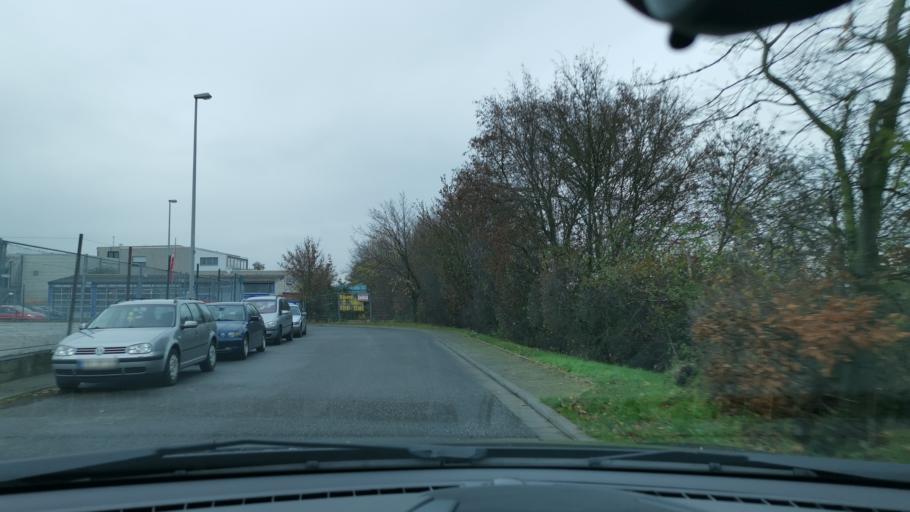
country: DE
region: North Rhine-Westphalia
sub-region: Regierungsbezirk Dusseldorf
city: Neubrueck
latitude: 51.1090
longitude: 6.6331
